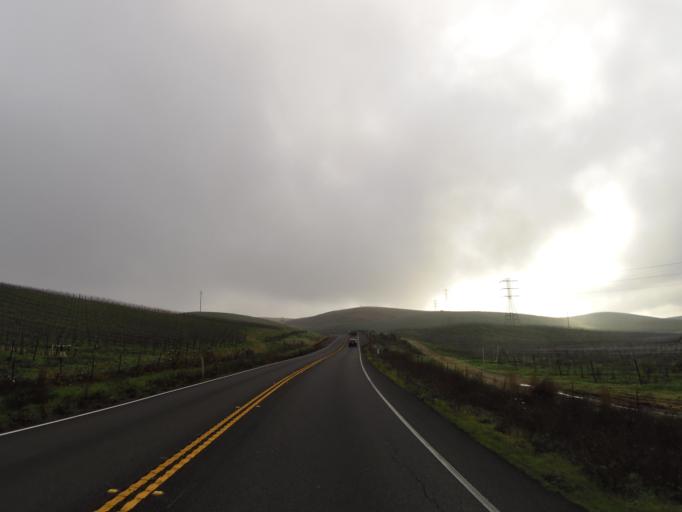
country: US
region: California
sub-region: Sonoma County
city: Sonoma
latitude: 38.2527
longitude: -122.4021
